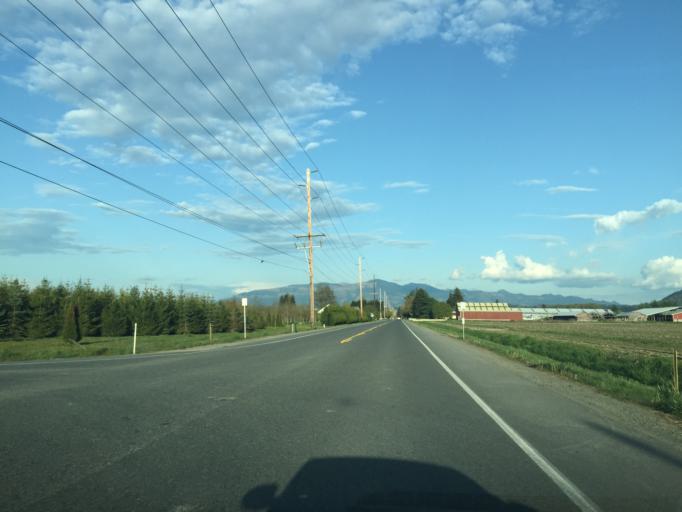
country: US
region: Washington
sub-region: Skagit County
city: Mount Vernon
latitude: 48.4209
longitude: -122.3791
